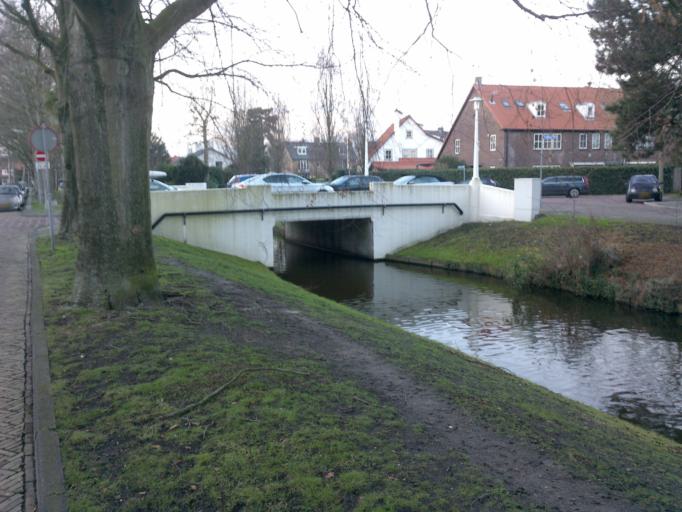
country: NL
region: North Holland
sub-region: Gemeente Bloemendaal
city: Bennebroek
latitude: 52.3263
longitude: 4.5928
